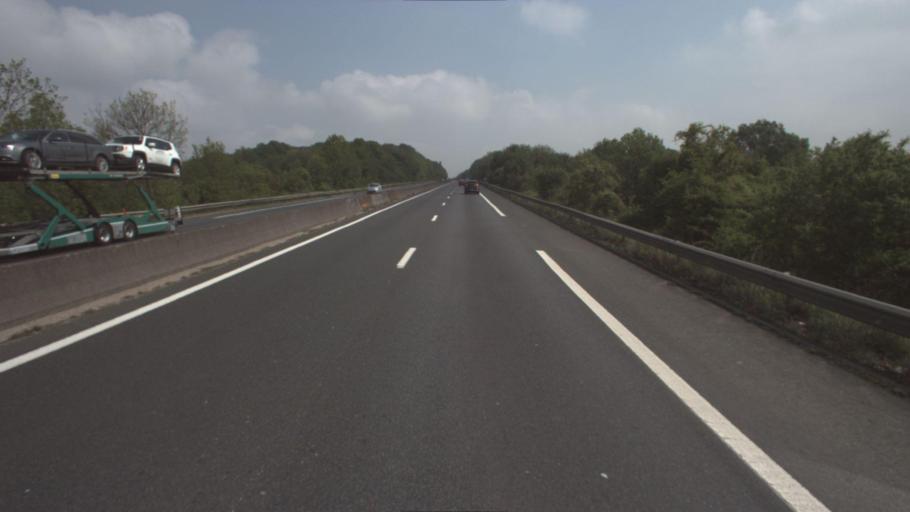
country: FR
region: Ile-de-France
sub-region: Departement de Seine-et-Marne
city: Saint-Mard
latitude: 49.0425
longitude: 2.6869
